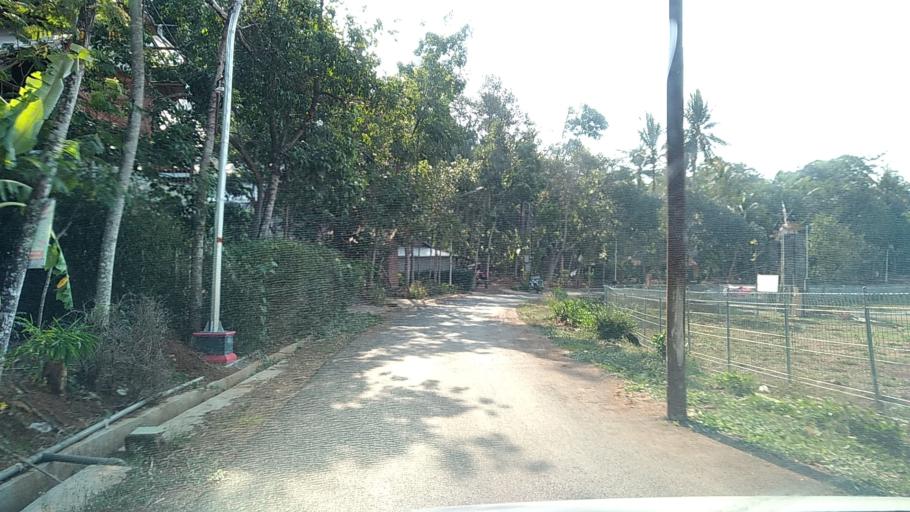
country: ID
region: Central Java
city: Ungaran
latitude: -7.0648
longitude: 110.3470
